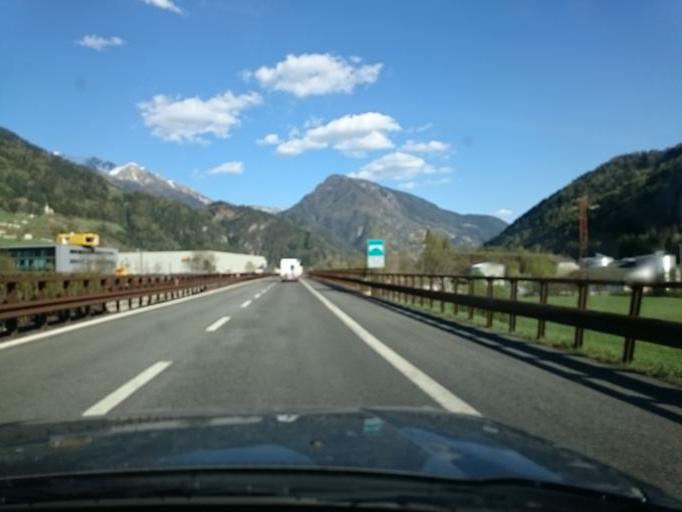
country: IT
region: Trentino-Alto Adige
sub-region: Bolzano
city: Campo di Trens
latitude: 46.8671
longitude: 11.4881
